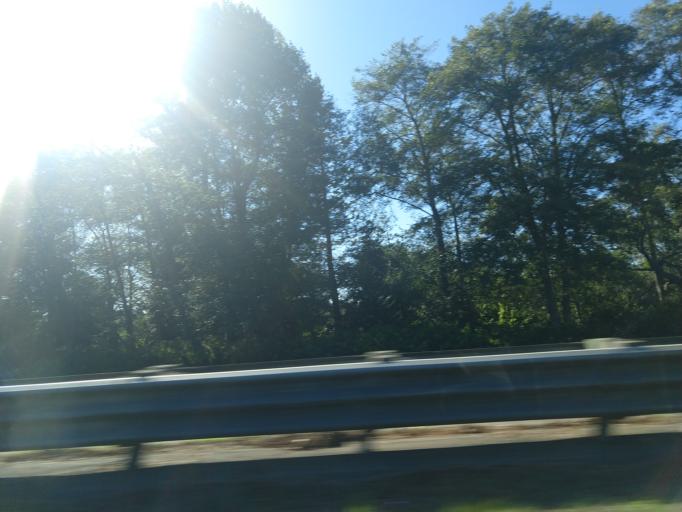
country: US
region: California
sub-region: Humboldt County
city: Fortuna
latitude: 40.5818
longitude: -124.1512
